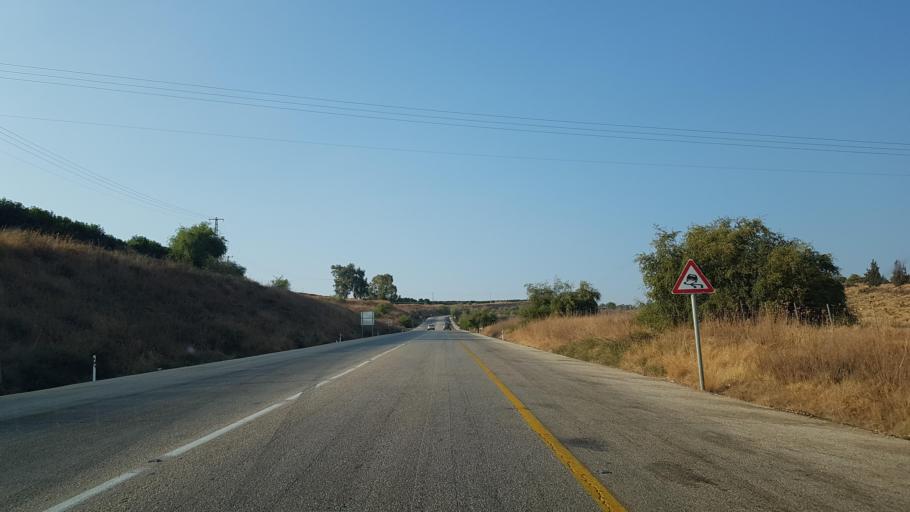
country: SY
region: Quneitra
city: Al Butayhah
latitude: 32.8942
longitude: 35.5979
